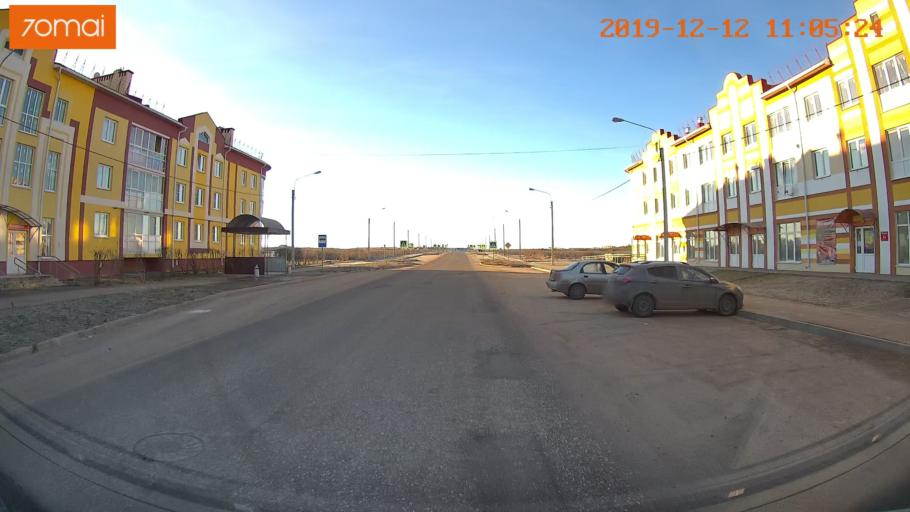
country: RU
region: Ivanovo
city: Kokhma
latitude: 56.9494
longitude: 41.0991
